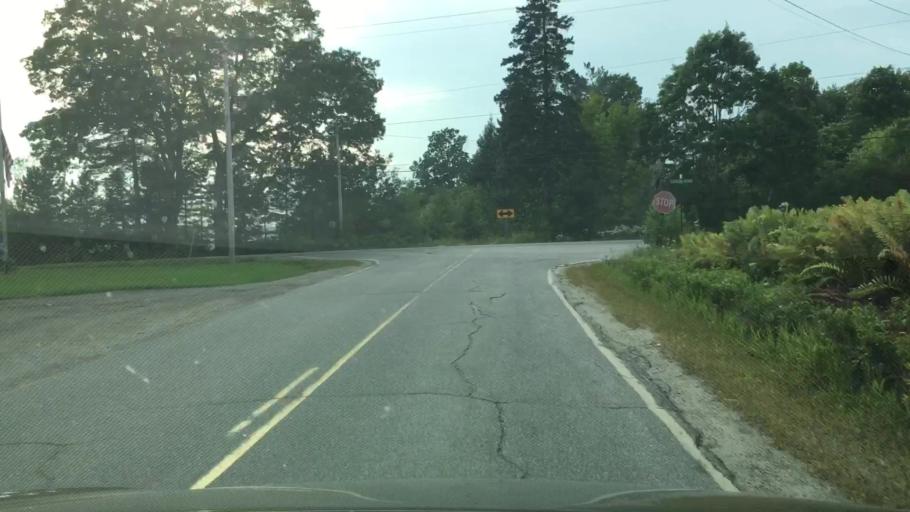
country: US
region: Maine
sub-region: Hancock County
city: Penobscot
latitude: 44.4742
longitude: -68.7789
